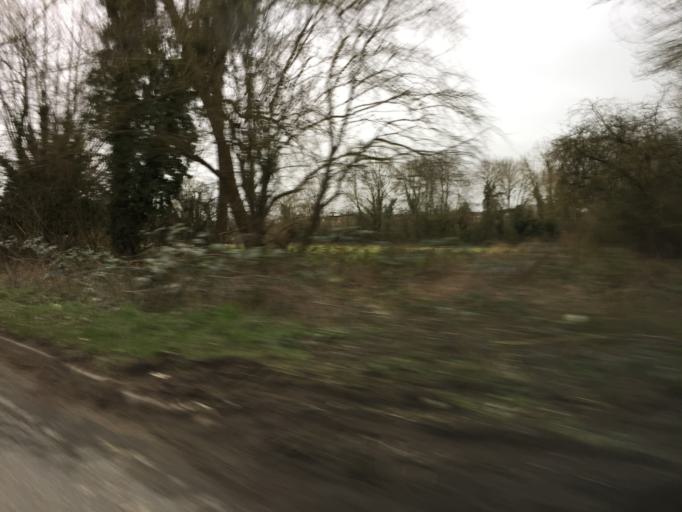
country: GB
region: England
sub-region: Oxfordshire
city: Wantage
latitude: 51.5939
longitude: -1.4573
